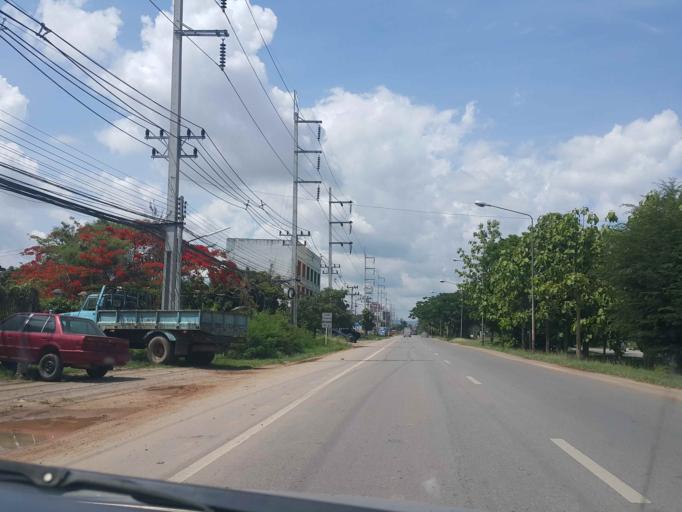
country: TH
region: Phayao
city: Phayao
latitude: 19.1535
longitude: 99.9131
